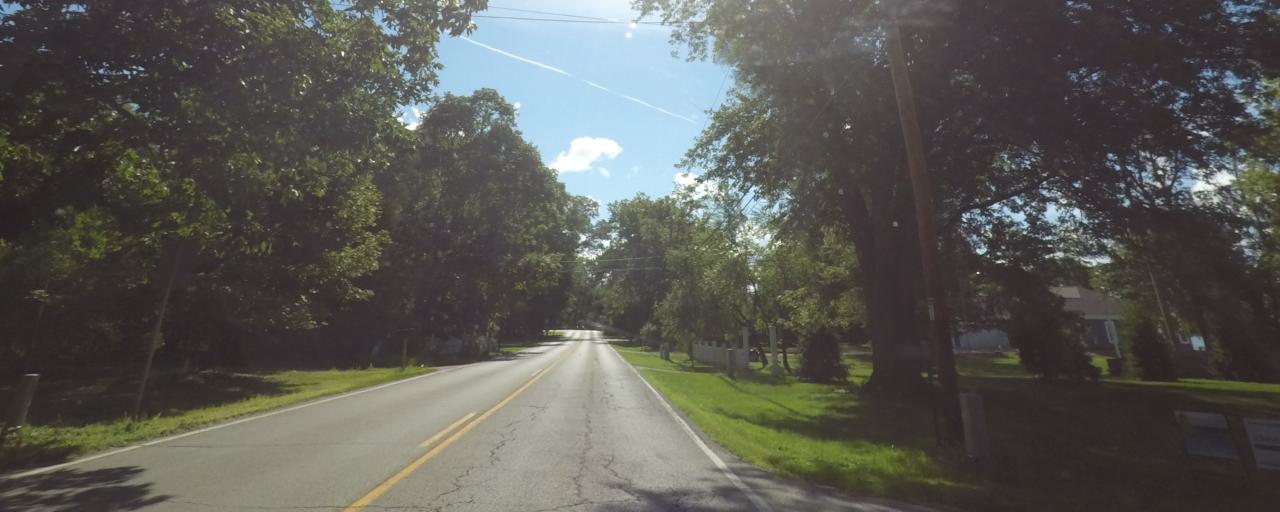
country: US
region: Wisconsin
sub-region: Waukesha County
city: Oconomowoc
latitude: 43.0821
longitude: -88.4977
